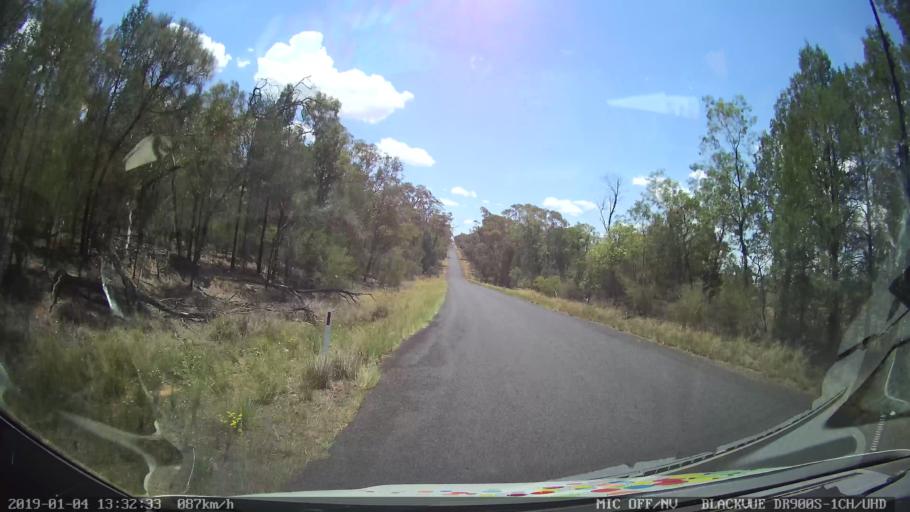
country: AU
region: New South Wales
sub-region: Dubbo Municipality
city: Eulomogo
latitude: -32.6081
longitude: 148.5478
